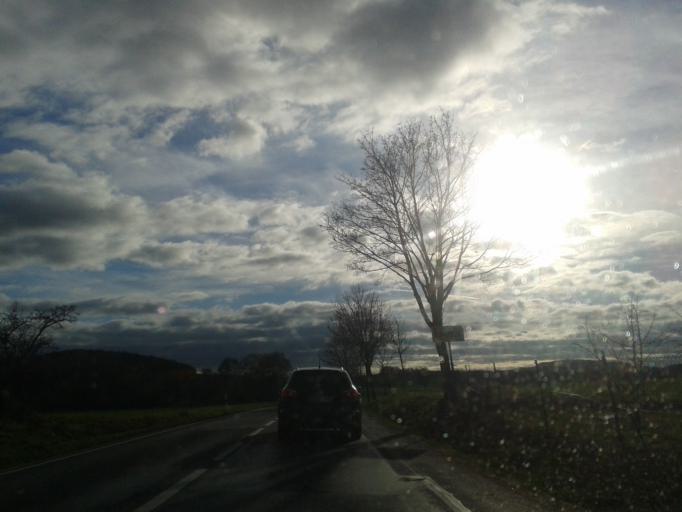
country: DE
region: Saxony
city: Weissenberg
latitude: 51.1876
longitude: 14.6417
